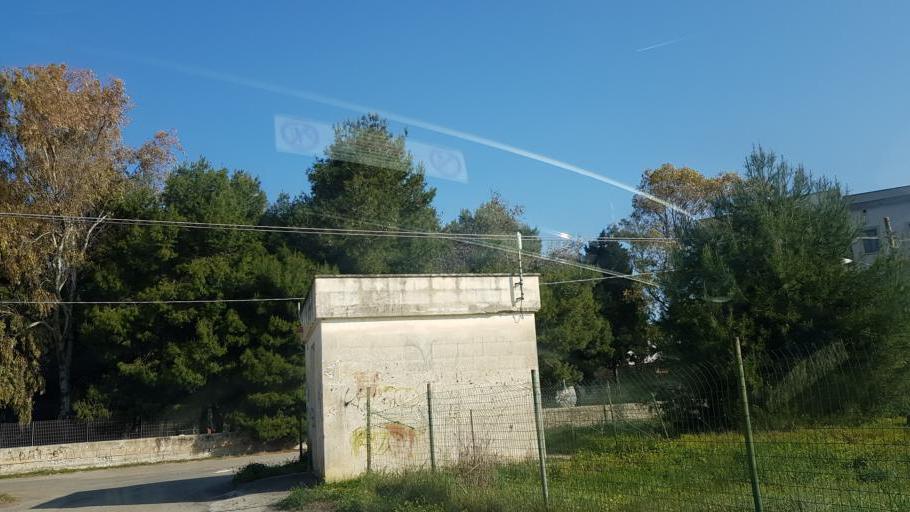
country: IT
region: Apulia
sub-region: Provincia di Brindisi
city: Materdomini
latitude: 40.6689
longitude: 17.9421
